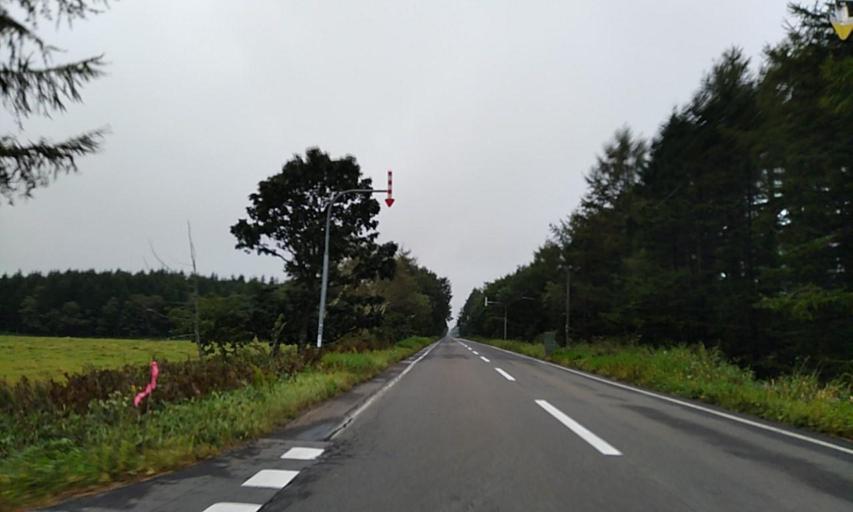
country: JP
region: Hokkaido
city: Shibetsu
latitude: 43.5029
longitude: 144.6587
